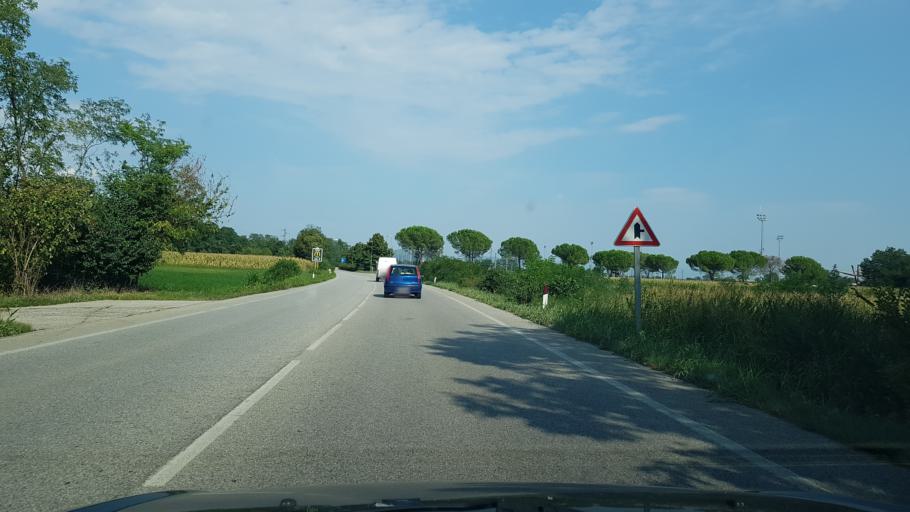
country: IT
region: Friuli Venezia Giulia
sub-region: Provincia di Udine
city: Passons
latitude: 46.0601
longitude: 13.1805
